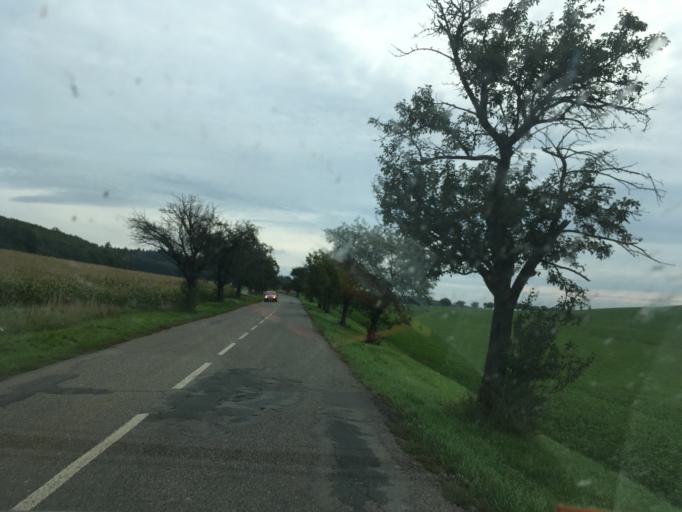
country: CZ
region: South Moravian
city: Oslavany
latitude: 49.1425
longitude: 16.2868
